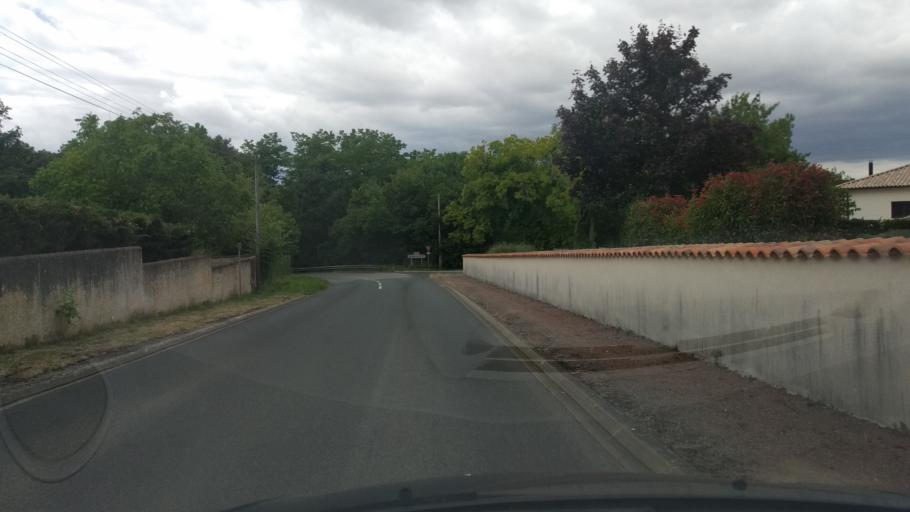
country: FR
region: Poitou-Charentes
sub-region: Departement de la Vienne
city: Vouille
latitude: 46.6322
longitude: 0.1768
